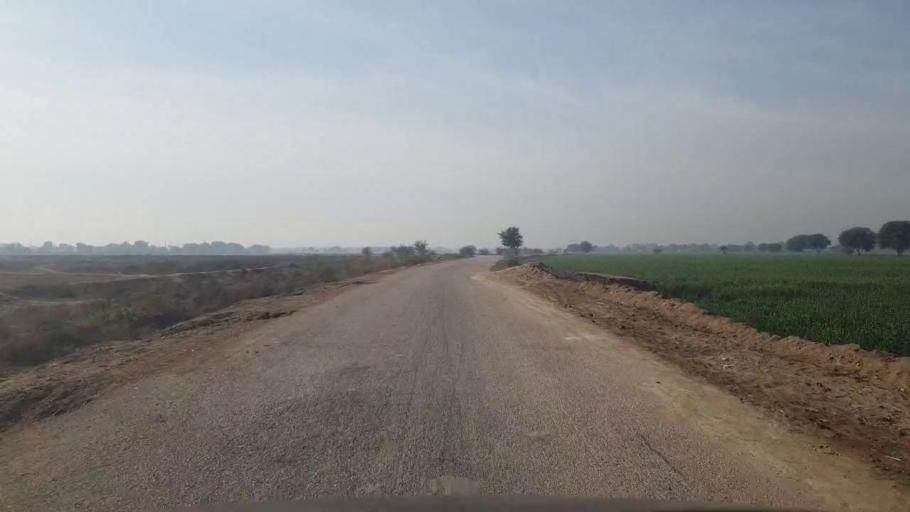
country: PK
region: Sindh
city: Umarkot
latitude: 25.3477
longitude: 69.6973
